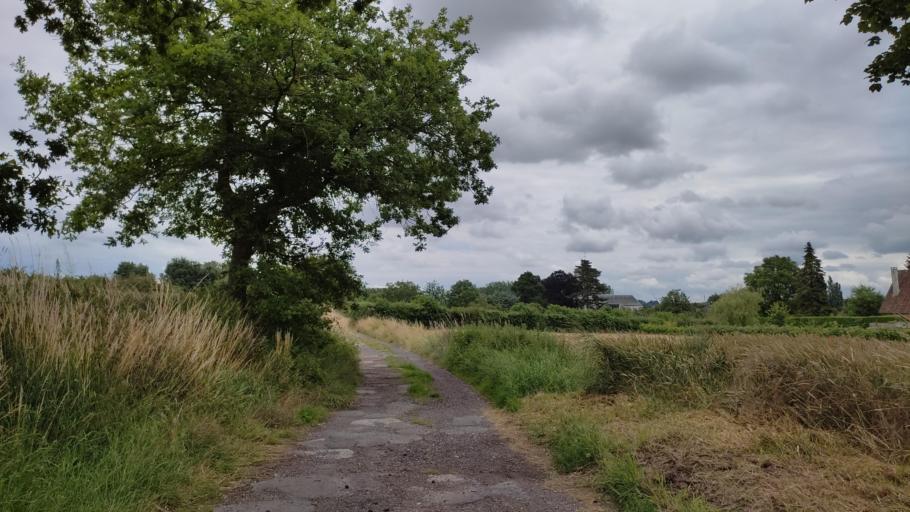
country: FR
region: Nord-Pas-de-Calais
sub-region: Departement du Pas-de-Calais
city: Riviere
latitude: 50.2349
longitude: 2.6818
